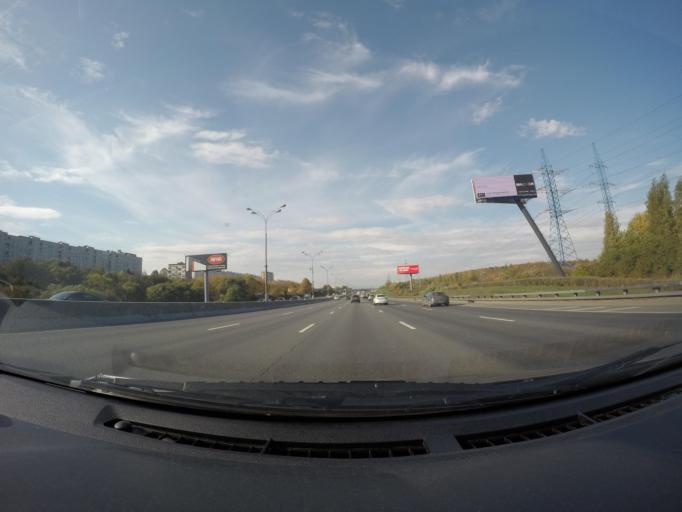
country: RU
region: Moscow
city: Bibirevo
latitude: 55.9006
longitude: 37.6246
